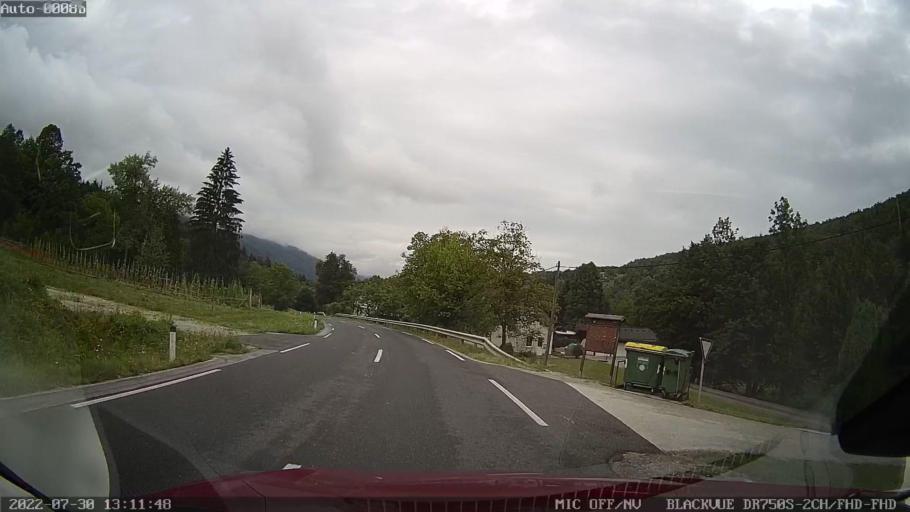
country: SI
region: Dolenjske Toplice
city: Dolenjske Toplice
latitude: 45.7062
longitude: 15.0751
